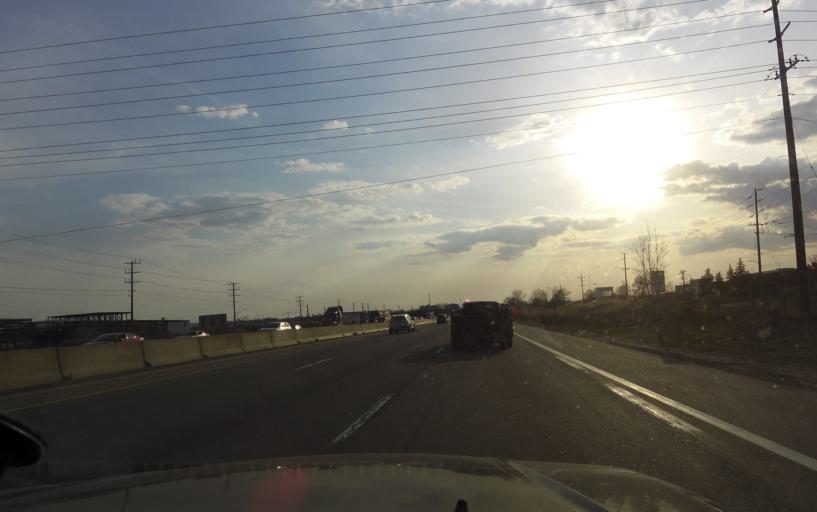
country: CA
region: Ontario
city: Oshawa
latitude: 43.8672
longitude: -78.9144
